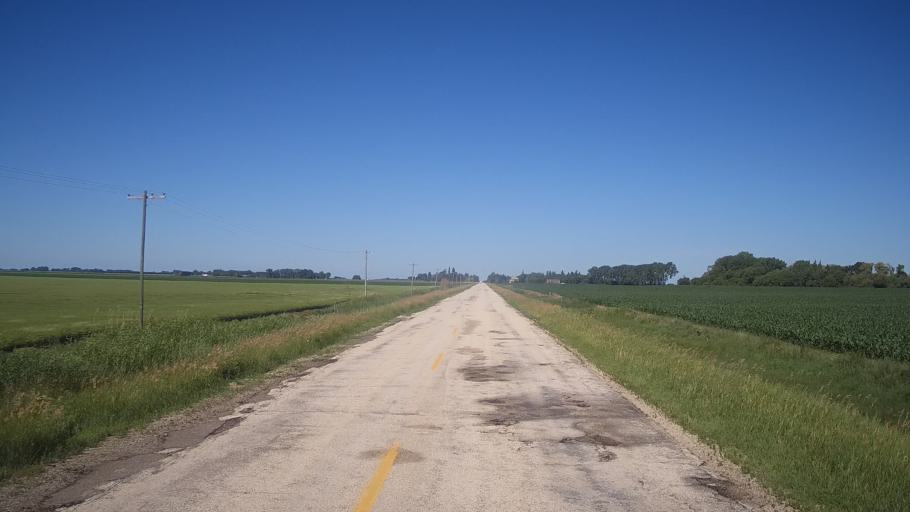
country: CA
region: Manitoba
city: Portage la Prairie
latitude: 50.0437
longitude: -98.0414
